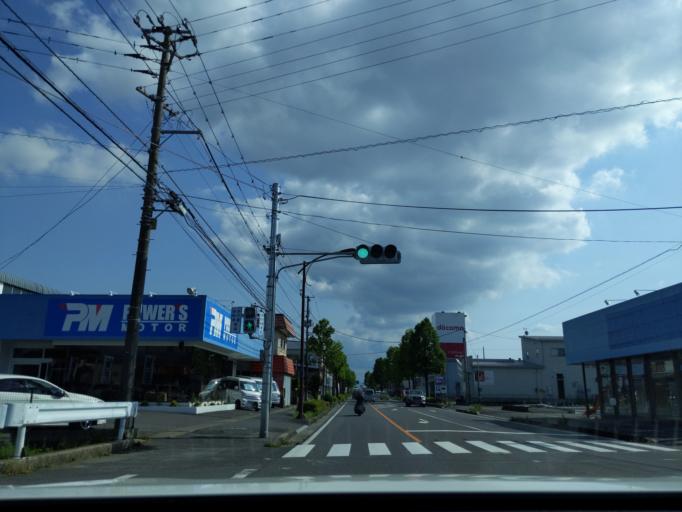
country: JP
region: Fukushima
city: Koriyama
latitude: 37.3762
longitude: 140.3843
